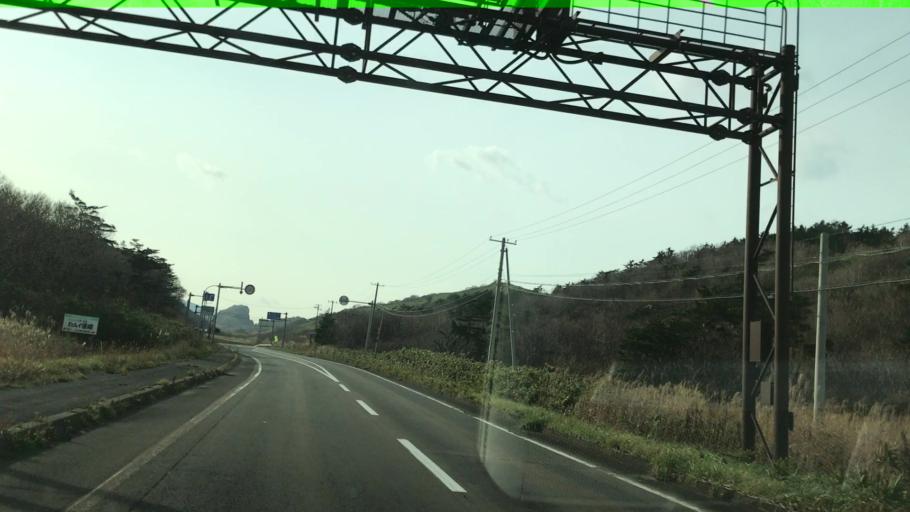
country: JP
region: Hokkaido
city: Iwanai
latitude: 43.3256
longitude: 140.3643
